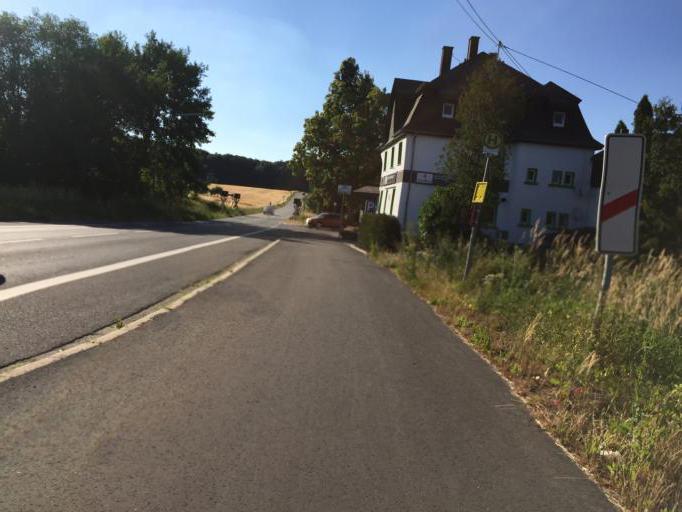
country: DE
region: Rheinland-Pfalz
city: Wallmerod
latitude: 50.4915
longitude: 7.9448
